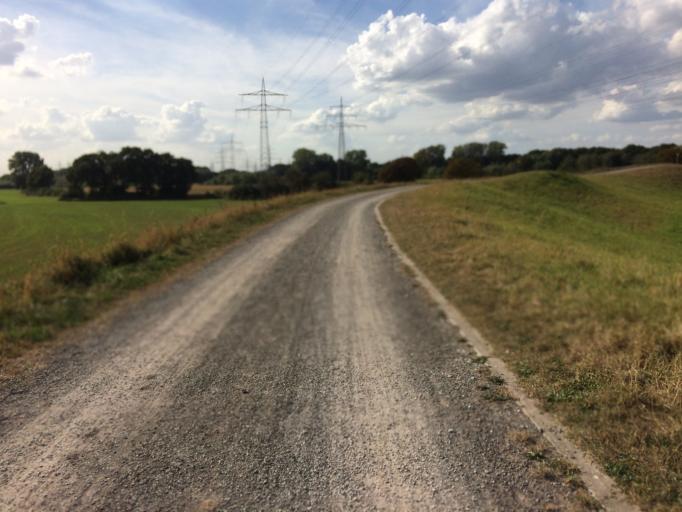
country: DE
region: North Rhine-Westphalia
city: Marl
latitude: 51.6996
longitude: 7.0824
